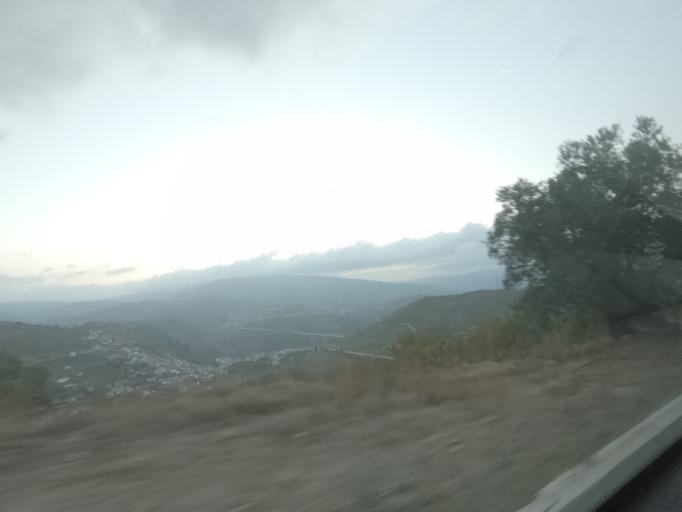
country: PT
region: Vila Real
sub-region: Peso da Regua
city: Peso da Regua
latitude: 41.1334
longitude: -7.7531
